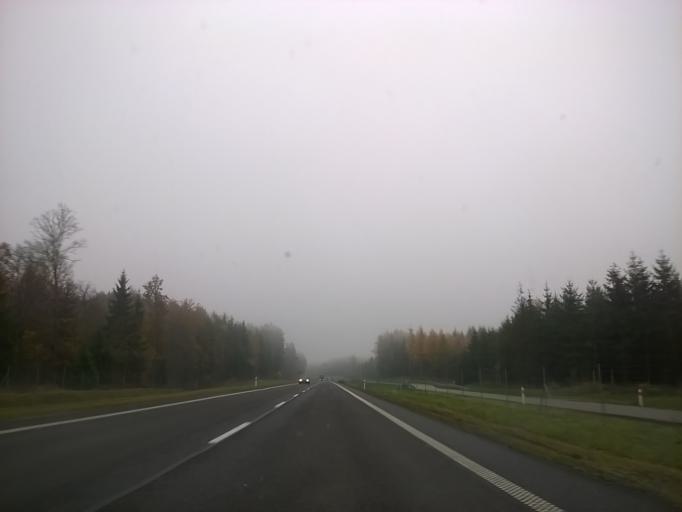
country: PL
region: Warmian-Masurian Voivodeship
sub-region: Powiat elblaski
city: Mlynary
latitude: 54.2523
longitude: 19.6903
